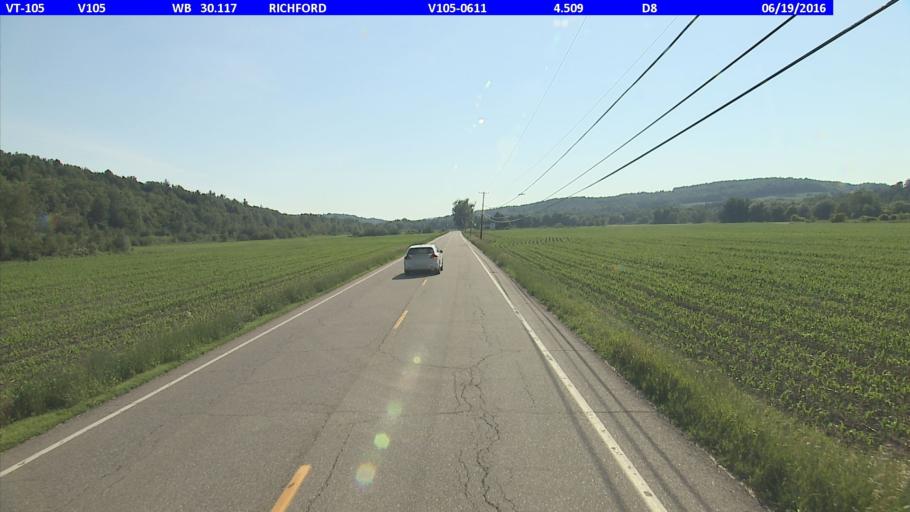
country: US
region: Vermont
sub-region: Franklin County
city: Richford
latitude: 44.9954
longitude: -72.6293
